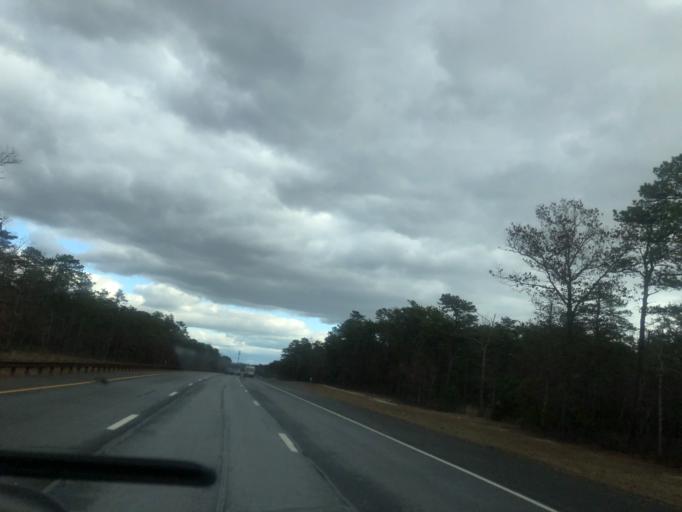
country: US
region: New Jersey
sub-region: Ocean County
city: Tuckerton
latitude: 39.6599
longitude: -74.3281
